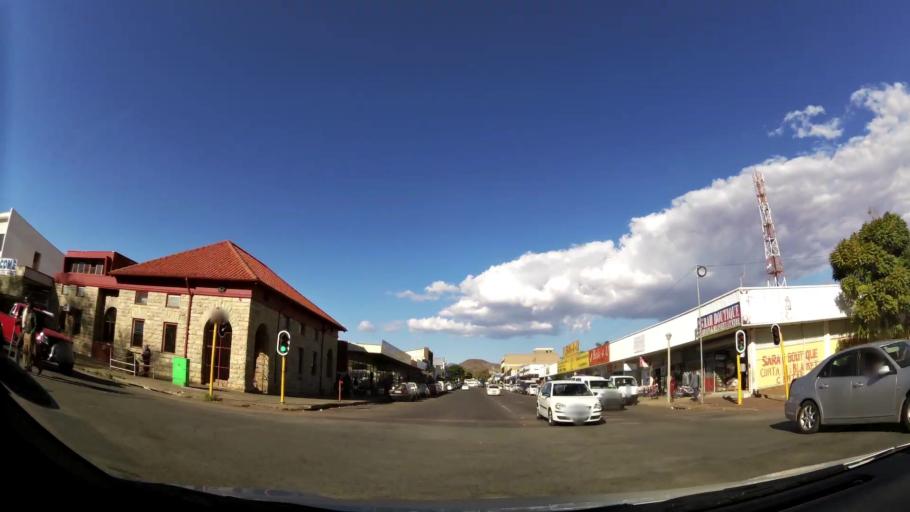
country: ZA
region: Limpopo
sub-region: Waterberg District Municipality
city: Mokopane
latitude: -24.1829
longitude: 29.0109
